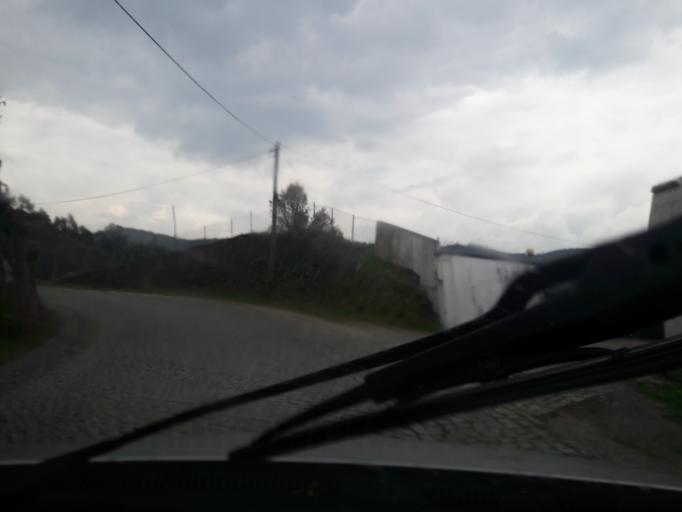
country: PT
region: Porto
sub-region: Amarante
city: Teloes
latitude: 41.3421
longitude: -8.0670
